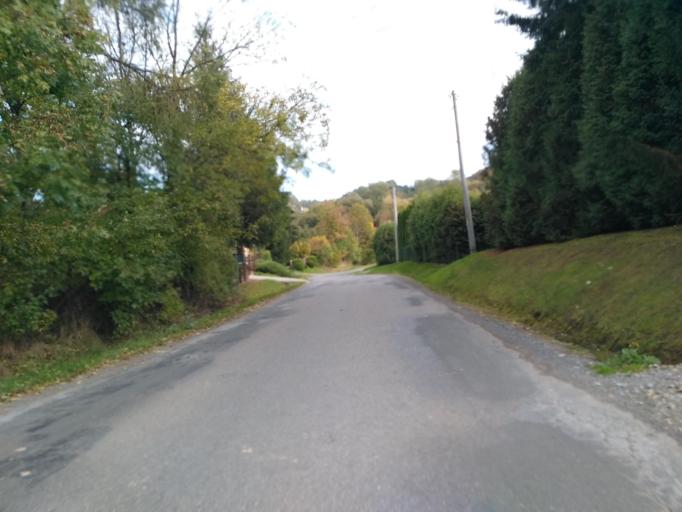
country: PL
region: Subcarpathian Voivodeship
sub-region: Powiat debicki
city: Jodlowa
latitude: 49.8930
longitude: 21.3303
